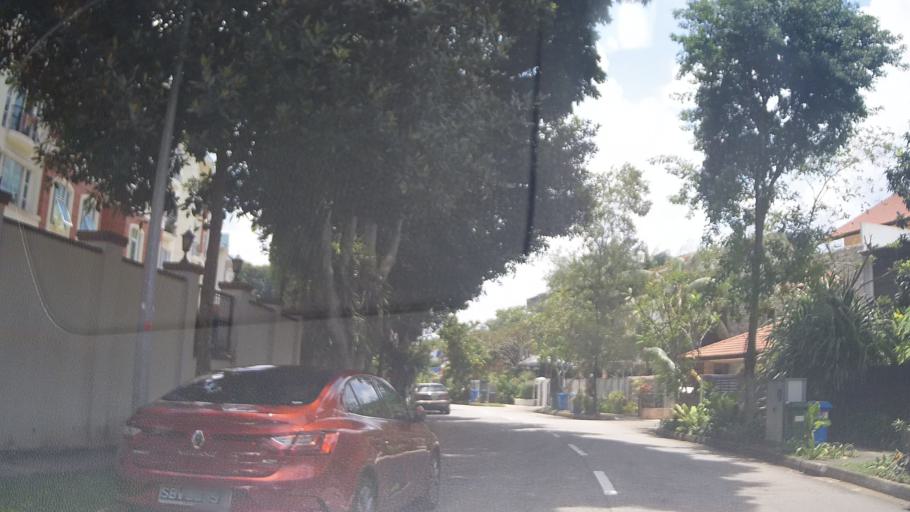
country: MY
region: Johor
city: Kampung Pasir Gudang Baru
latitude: 1.3902
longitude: 103.8565
